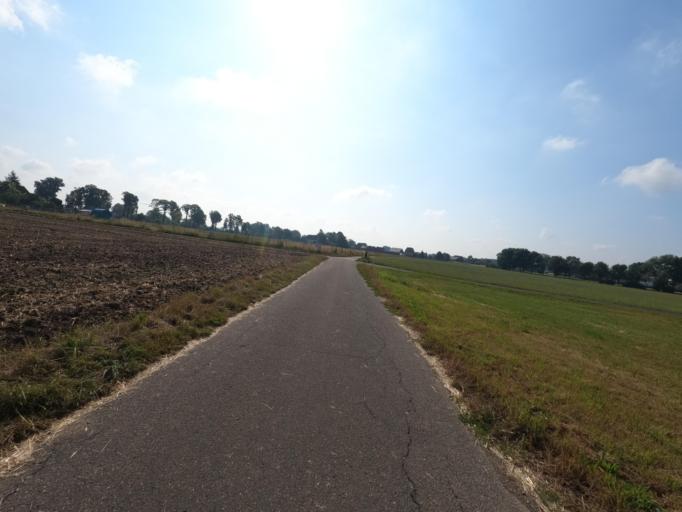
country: DE
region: North Rhine-Westphalia
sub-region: Regierungsbezirk Koln
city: Heinsberg
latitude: 51.0894
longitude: 6.0975
